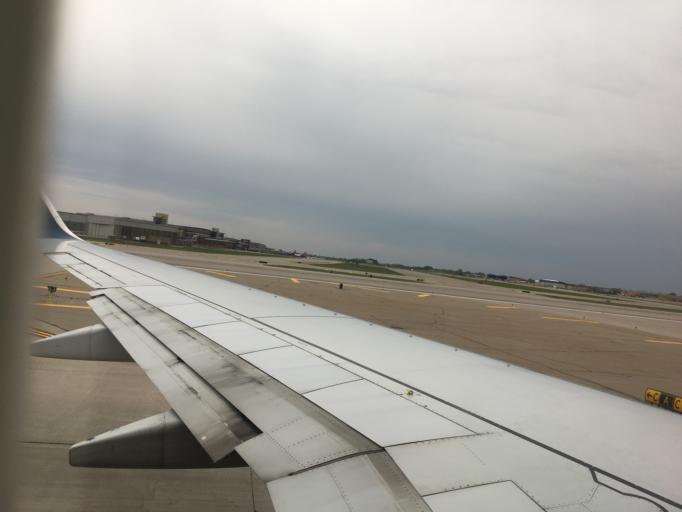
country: US
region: Minnesota
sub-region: Hennepin County
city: Richfield
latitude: 44.8829
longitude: -93.2199
